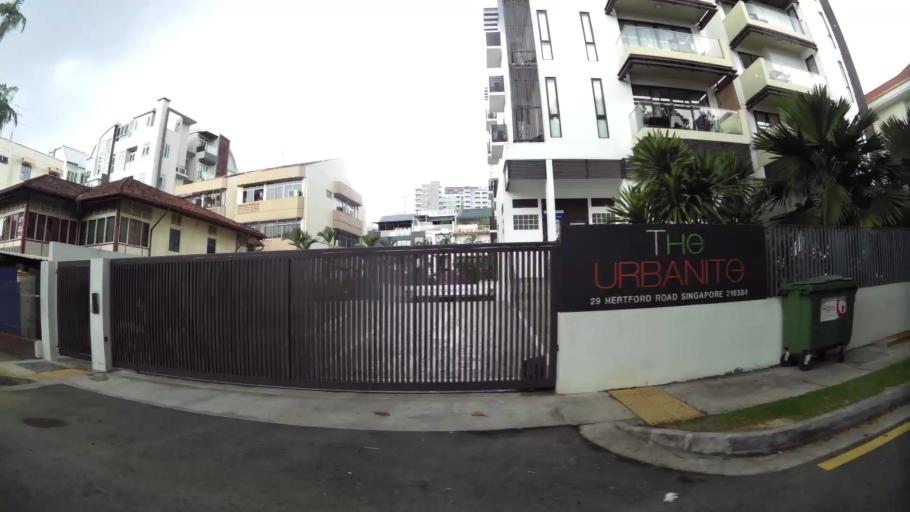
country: SG
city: Singapore
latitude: 1.3133
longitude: 103.8485
